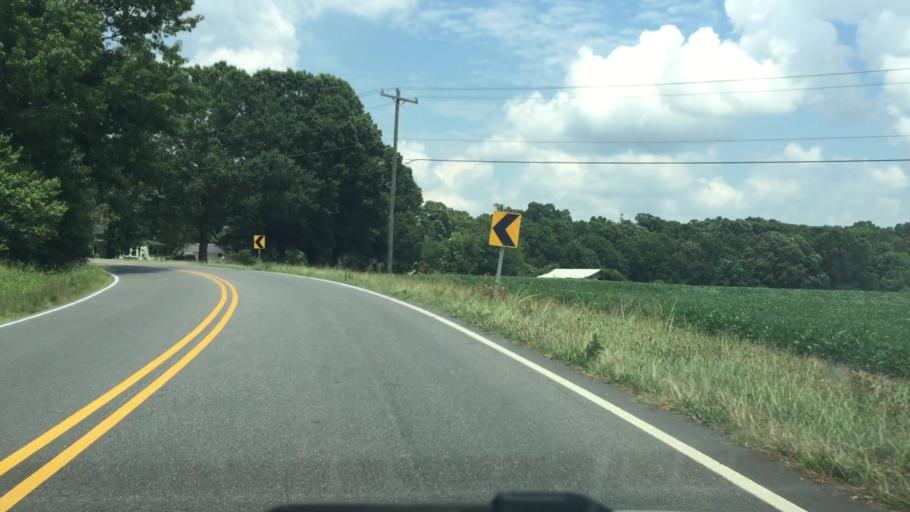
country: US
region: North Carolina
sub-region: Iredell County
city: Troutman
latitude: 35.7186
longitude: -80.8746
